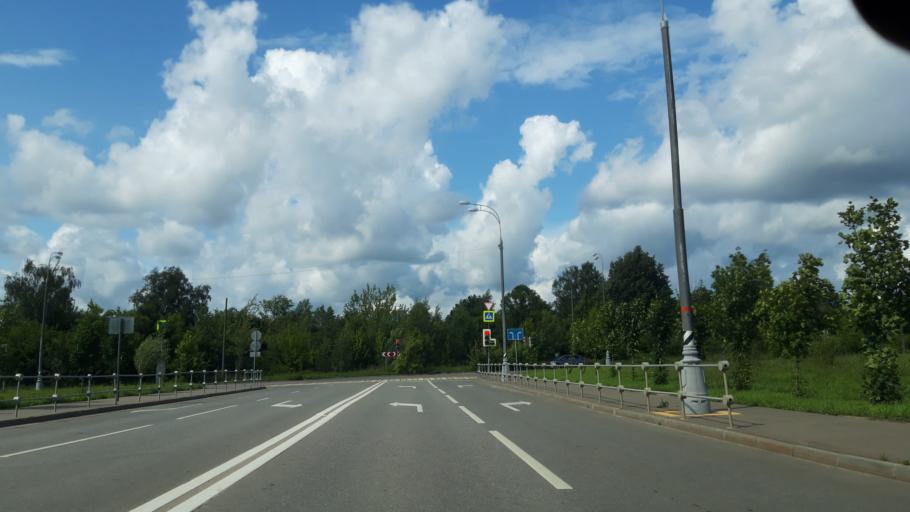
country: RU
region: Moscow
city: Zelenograd
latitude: 55.9703
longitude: 37.1888
